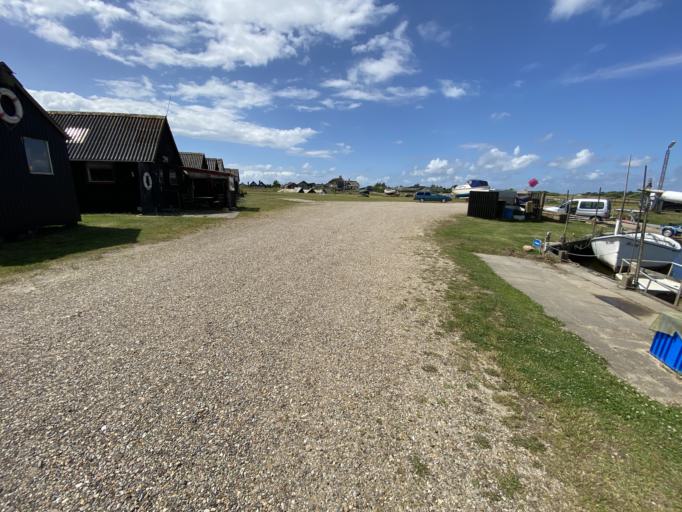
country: DK
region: Central Jutland
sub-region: Ringkobing-Skjern Kommune
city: Hvide Sande
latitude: 56.0535
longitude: 8.1269
